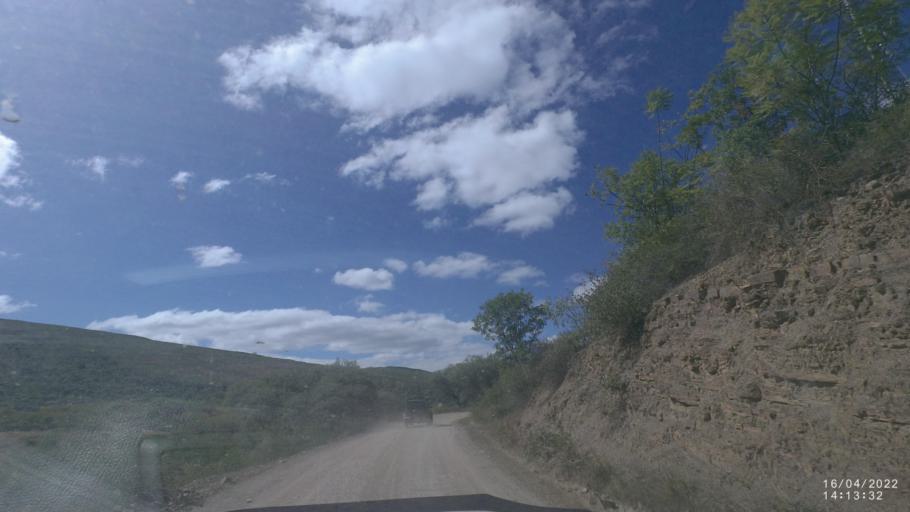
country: BO
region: Cochabamba
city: Mizque
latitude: -18.0588
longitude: -65.5096
